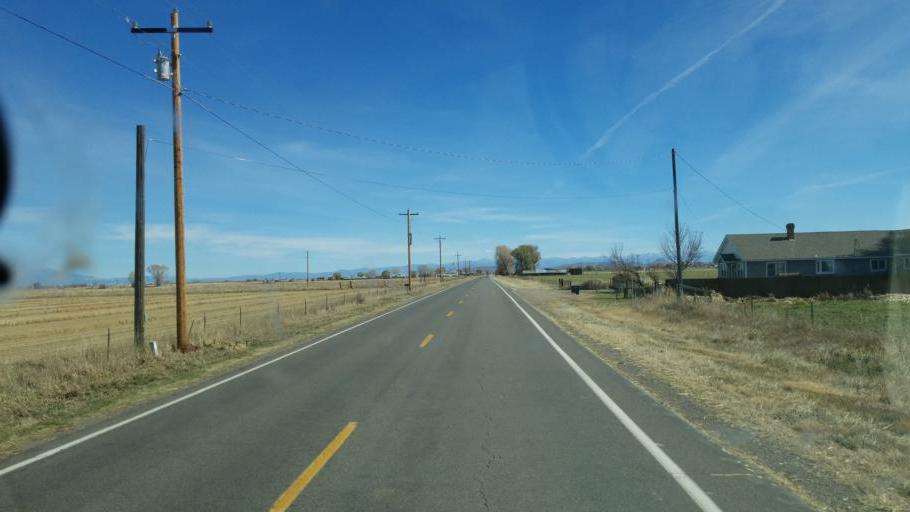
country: US
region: Colorado
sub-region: Conejos County
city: Conejos
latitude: 37.2836
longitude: -105.9889
